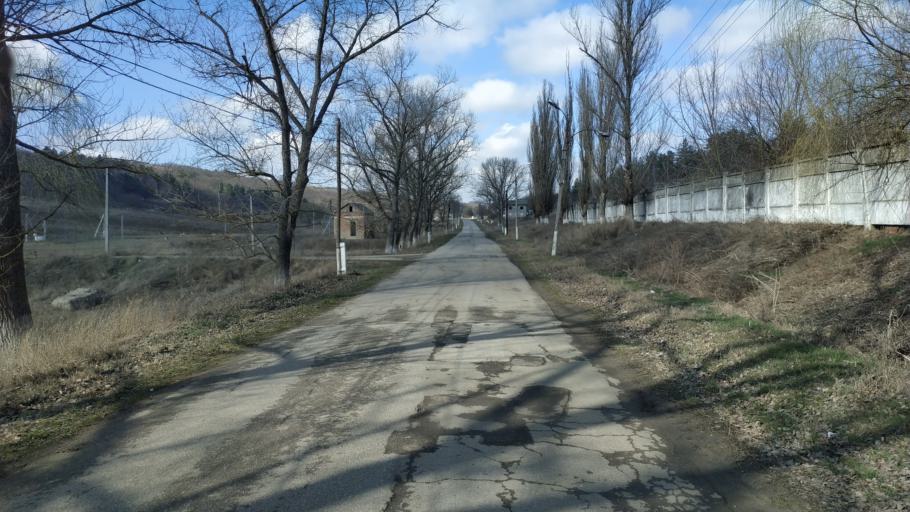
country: MD
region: Hincesti
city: Hincesti
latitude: 46.8700
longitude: 28.6375
